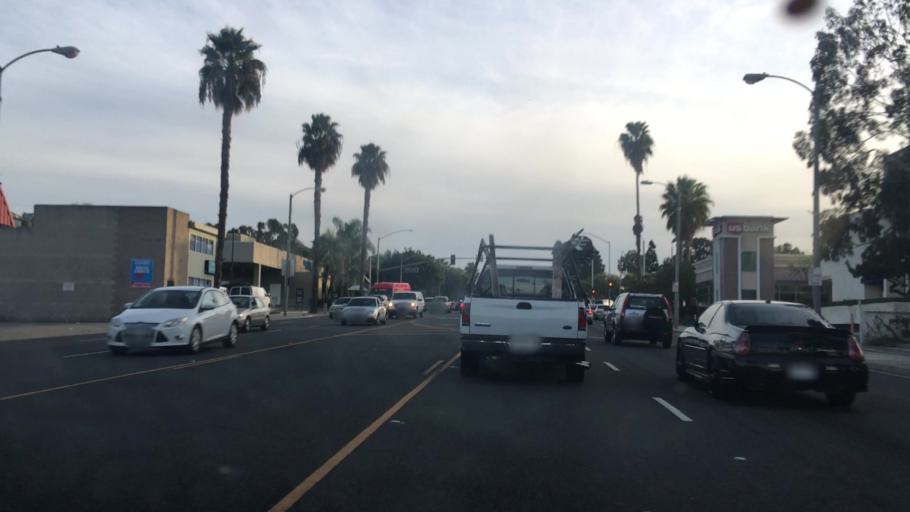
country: US
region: California
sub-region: Los Angeles County
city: Signal Hill
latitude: 33.8056
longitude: -118.1677
